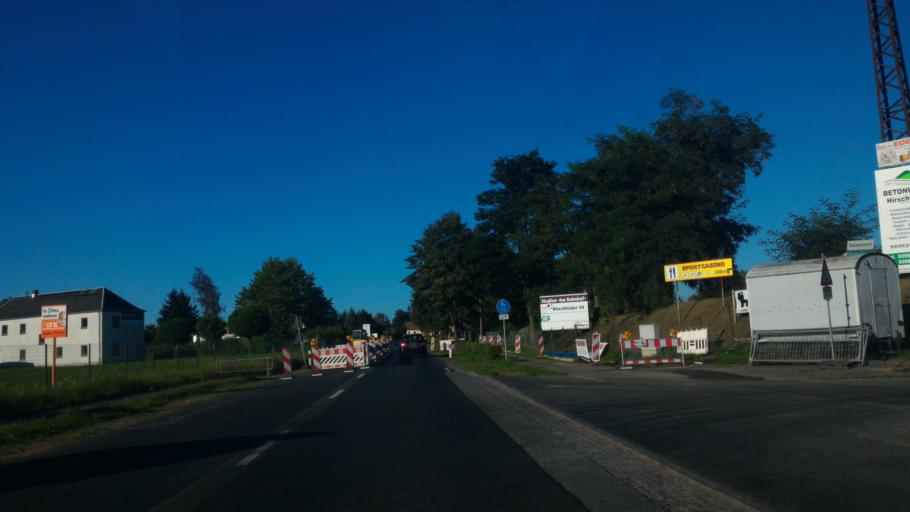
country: DE
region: Saxony
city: Hirschfelde
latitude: 50.9399
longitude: 14.8801
